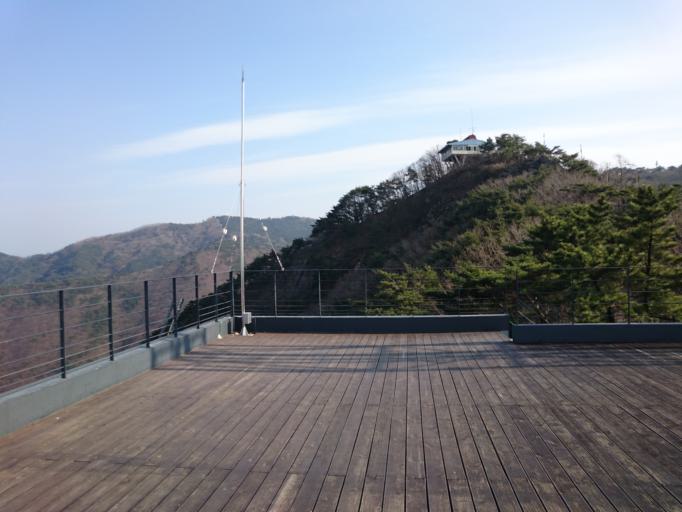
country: KR
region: Daegu
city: Daegu
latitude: 35.8224
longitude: 128.5793
